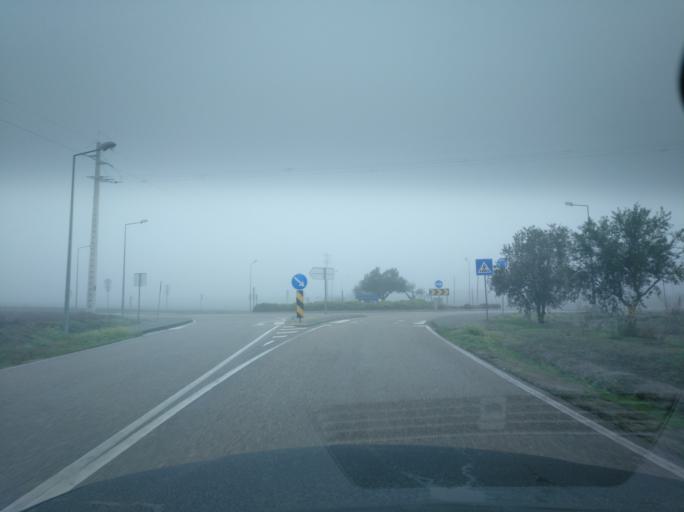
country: PT
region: Portalegre
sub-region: Campo Maior
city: Campo Maior
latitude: 39.0256
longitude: -7.0682
